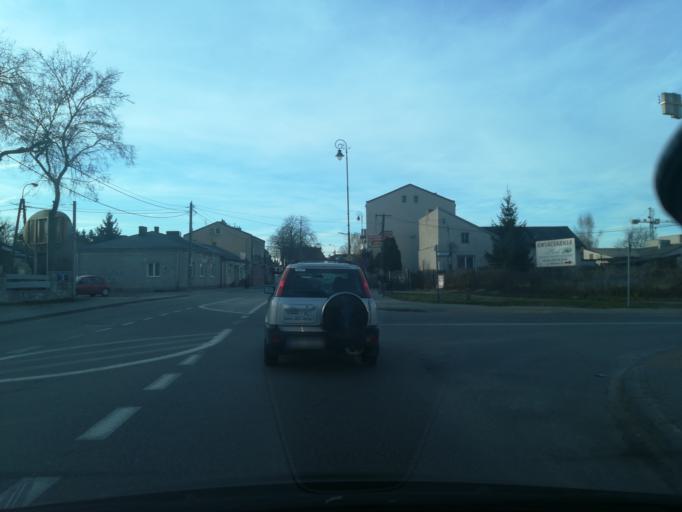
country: PL
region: Masovian Voivodeship
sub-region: Powiat piaseczynski
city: Konstancin-Jeziorna
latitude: 52.0921
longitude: 21.1192
